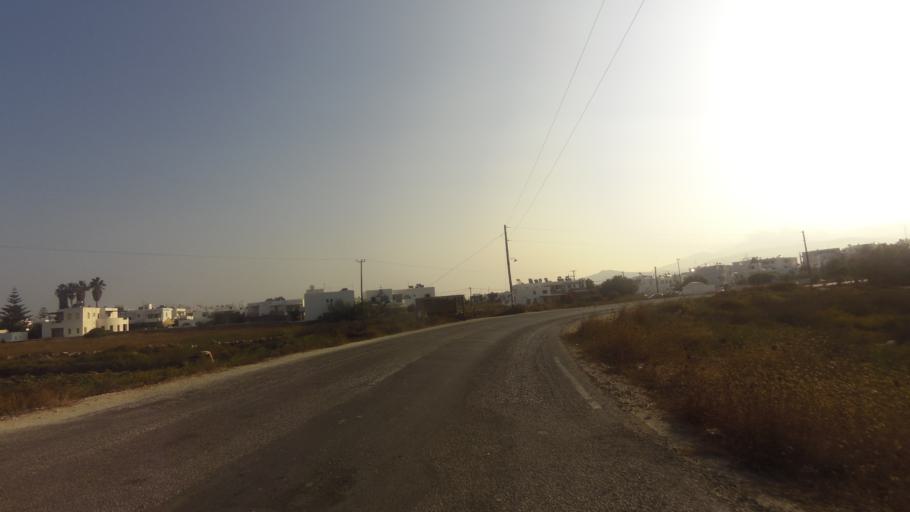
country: GR
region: South Aegean
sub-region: Nomos Kykladon
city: Antiparos
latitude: 37.0377
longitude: 25.0811
